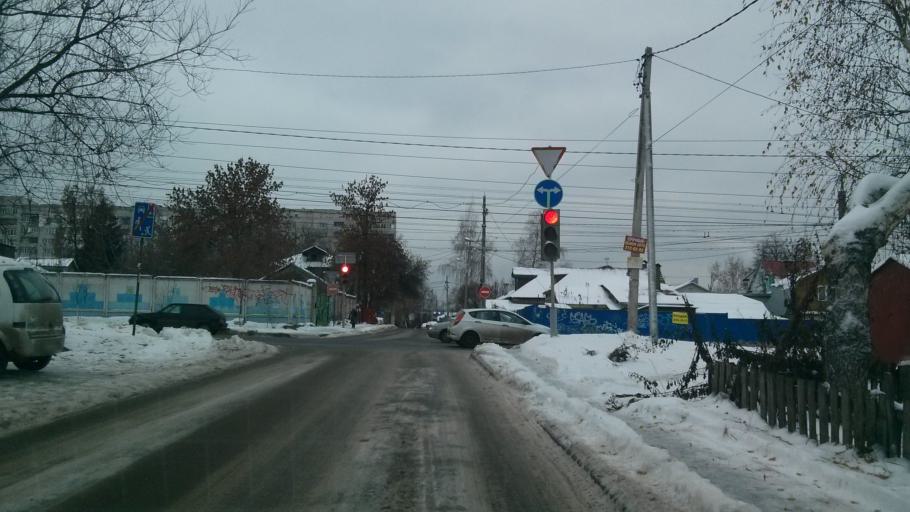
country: RU
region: Nizjnij Novgorod
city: Nizhniy Novgorod
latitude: 56.3031
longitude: 44.0295
